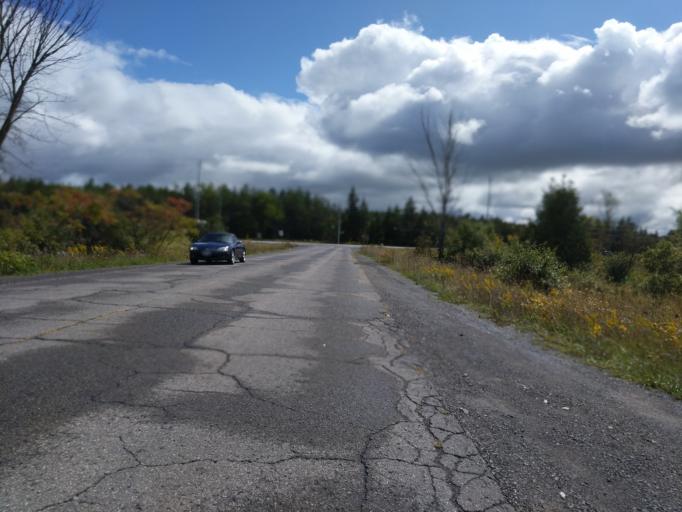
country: CA
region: Ontario
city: Bells Corners
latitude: 45.3119
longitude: -75.8607
